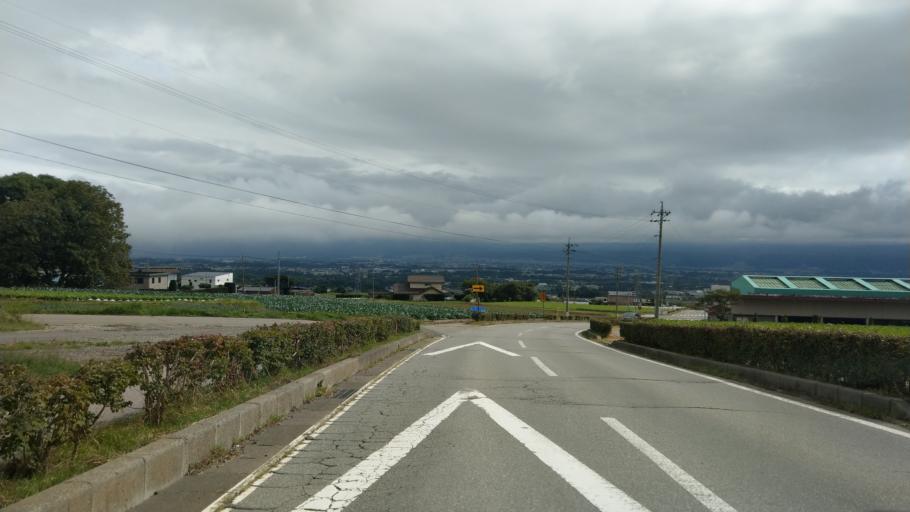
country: JP
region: Nagano
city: Komoro
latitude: 36.3355
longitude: 138.4582
